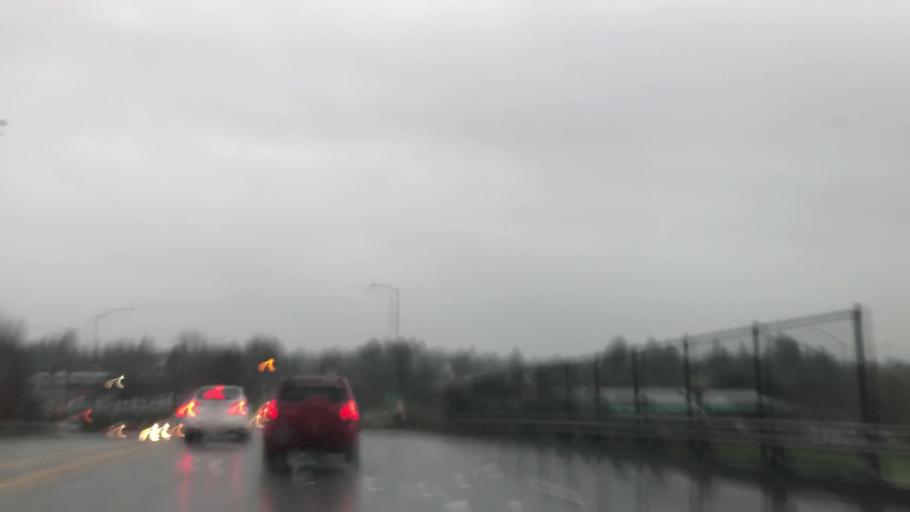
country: US
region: Oregon
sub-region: Washington County
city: Beaverton
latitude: 45.4766
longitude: -122.7900
